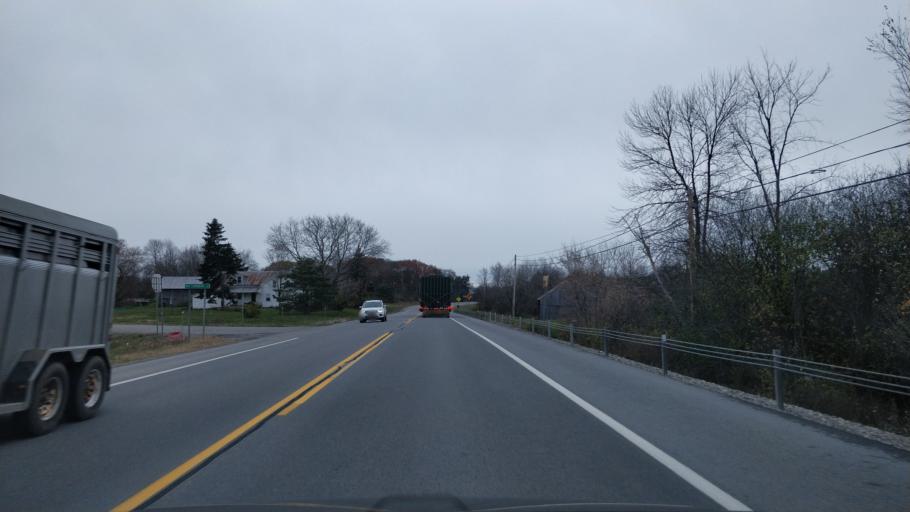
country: CA
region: Ontario
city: Brockville
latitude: 44.6164
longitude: -75.5969
